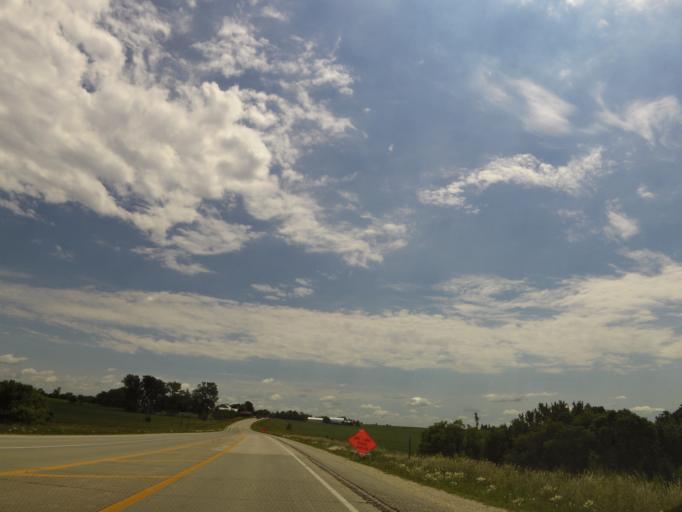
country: US
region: Iowa
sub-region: Bremer County
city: Denver
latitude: 42.7145
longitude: -92.3339
